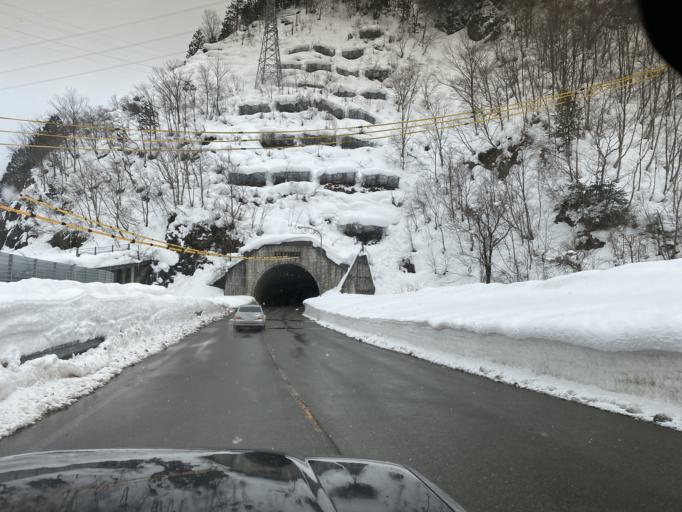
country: JP
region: Gifu
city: Takayama
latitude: 36.1265
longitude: 136.9061
